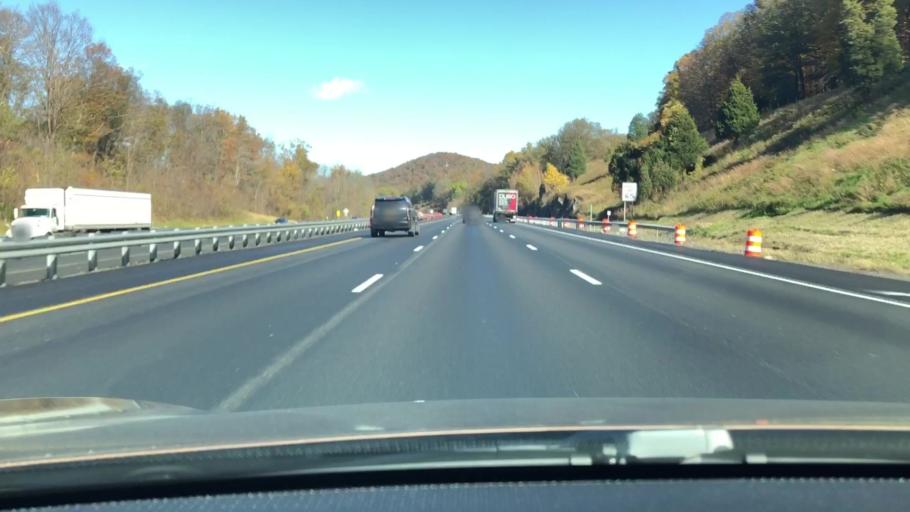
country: US
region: New York
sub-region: Orange County
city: Harriman
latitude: 41.2543
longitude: -74.1627
